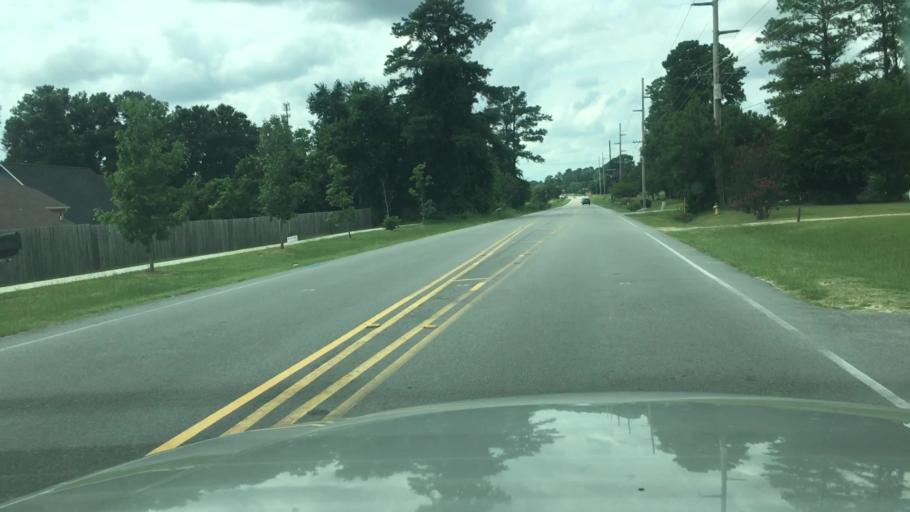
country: US
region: North Carolina
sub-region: Hoke County
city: Rockfish
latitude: 35.0098
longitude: -79.0026
